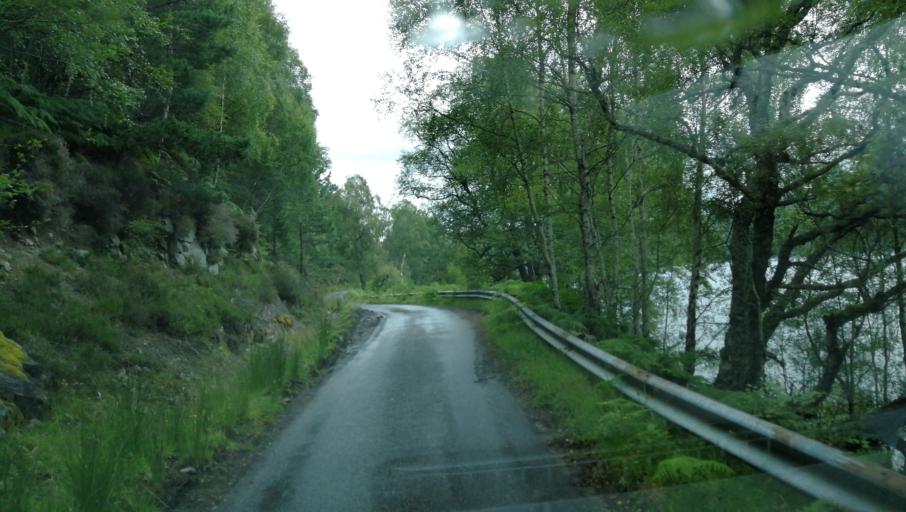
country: GB
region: Scotland
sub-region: Highland
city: Spean Bridge
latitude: 57.2753
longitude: -4.9537
